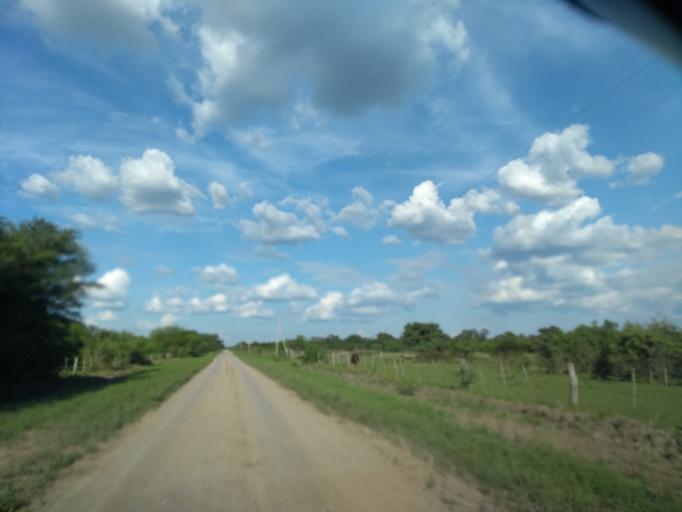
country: AR
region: Chaco
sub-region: Departamento de Quitilipi
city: Quitilipi
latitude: -26.7742
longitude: -60.1942
